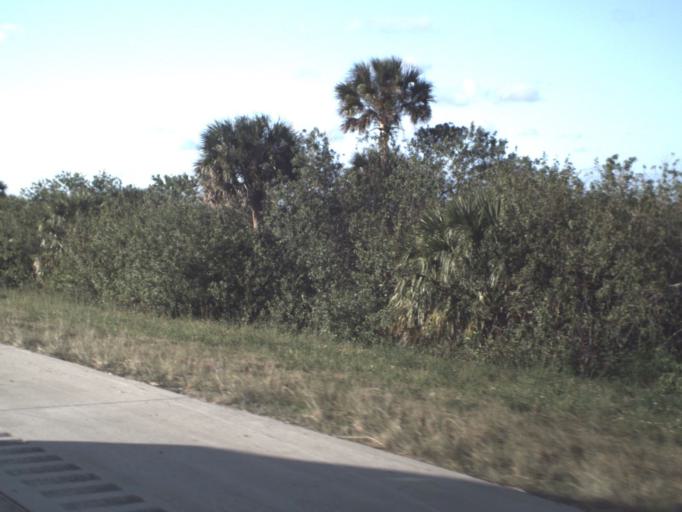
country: US
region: Florida
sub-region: Brevard County
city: Cocoa West
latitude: 28.3100
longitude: -80.7617
